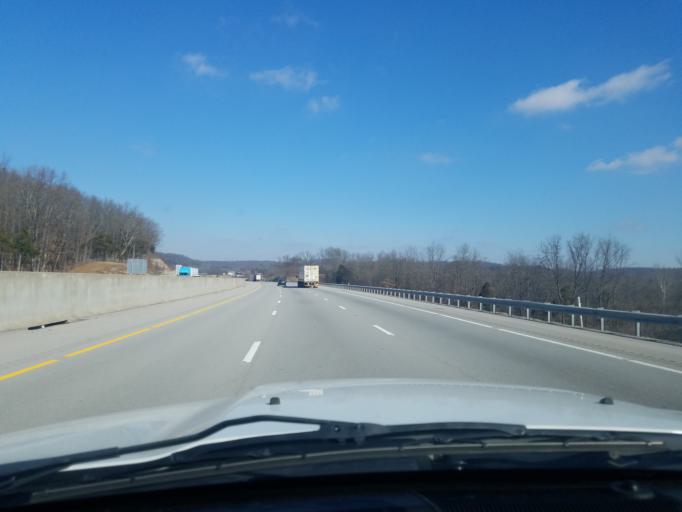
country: US
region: Kentucky
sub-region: Barren County
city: Cave City
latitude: 37.1439
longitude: -85.9716
